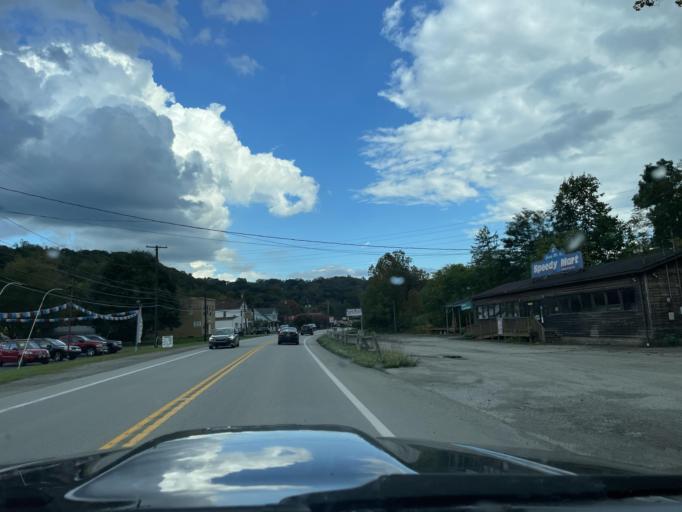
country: US
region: Pennsylvania
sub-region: Westmoreland County
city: Lower Burrell
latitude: 40.5497
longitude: -79.7382
